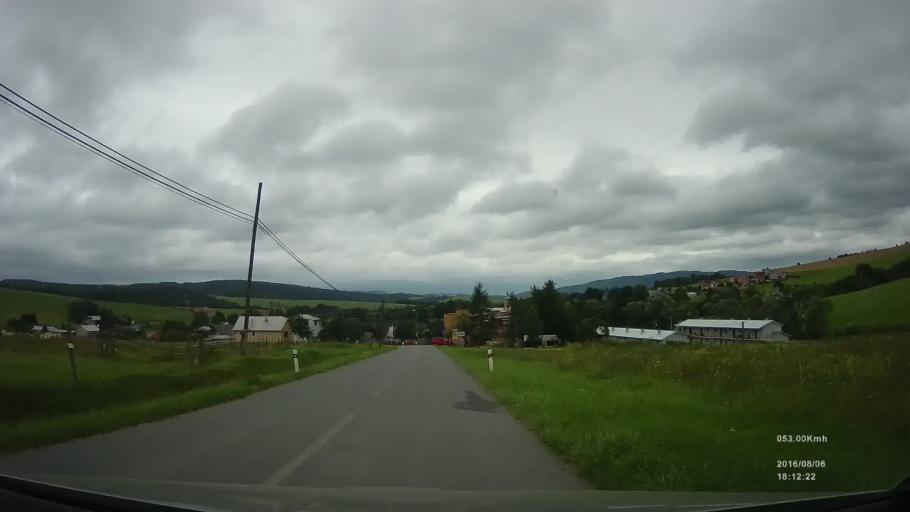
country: SK
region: Presovsky
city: Svidnik
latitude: 49.3644
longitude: 21.5773
